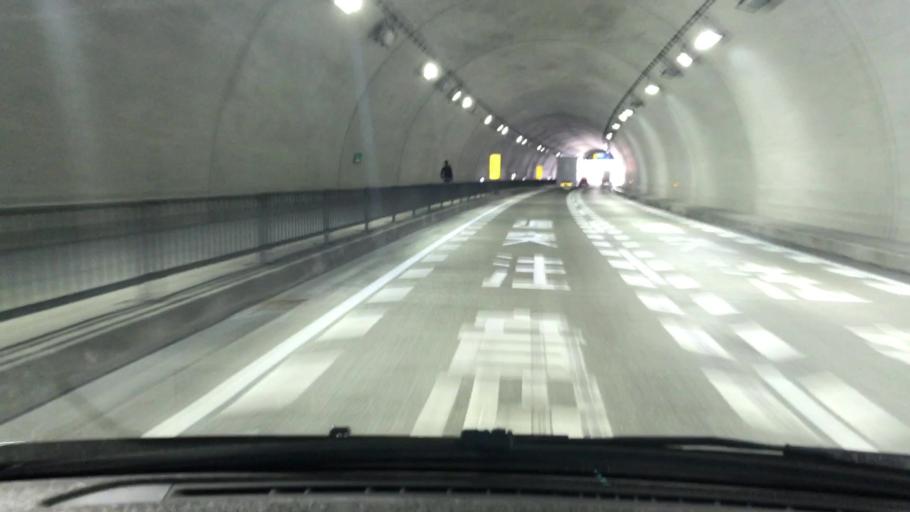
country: JP
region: Hyogo
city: Takarazuka
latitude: 34.8281
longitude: 135.3024
